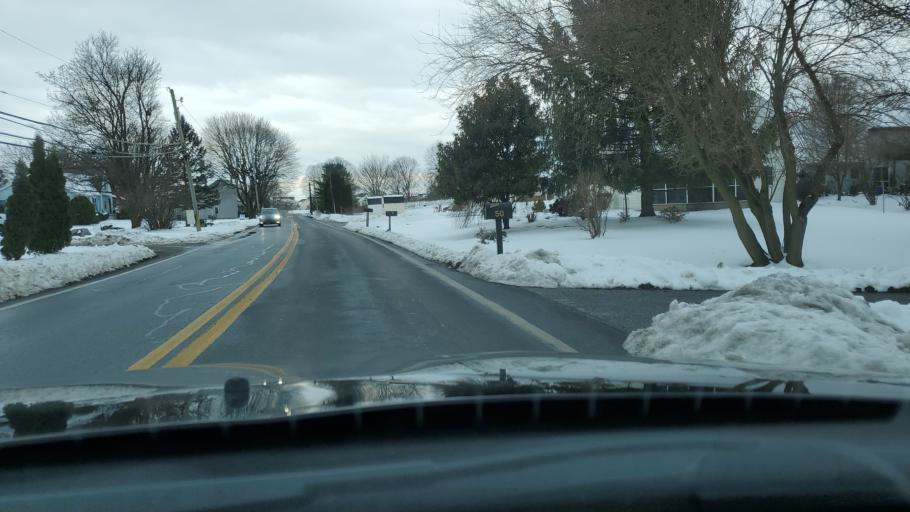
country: US
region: Pennsylvania
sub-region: Cumberland County
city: Mechanicsburg
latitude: 40.2104
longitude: -77.0355
